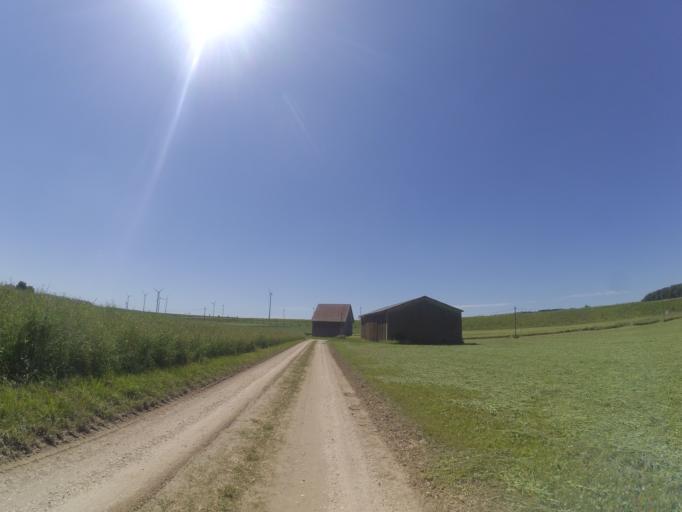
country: DE
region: Baden-Wuerttemberg
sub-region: Tuebingen Region
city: Lonsee
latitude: 48.4899
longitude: 9.8574
